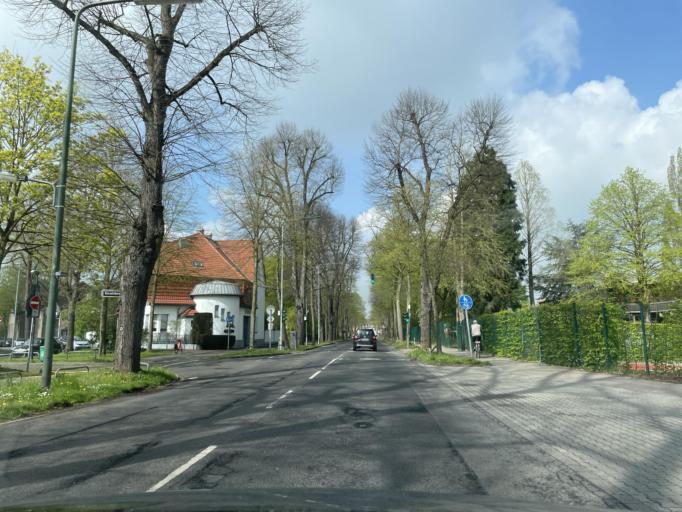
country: DE
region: North Rhine-Westphalia
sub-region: Regierungsbezirk Dusseldorf
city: Meerbusch
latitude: 51.3050
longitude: 6.7476
